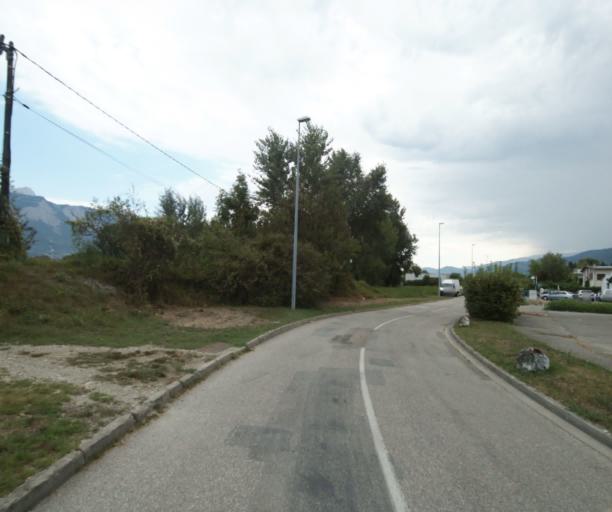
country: FR
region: Rhone-Alpes
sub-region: Departement de l'Isere
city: Domene
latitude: 45.1973
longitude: 5.8171
